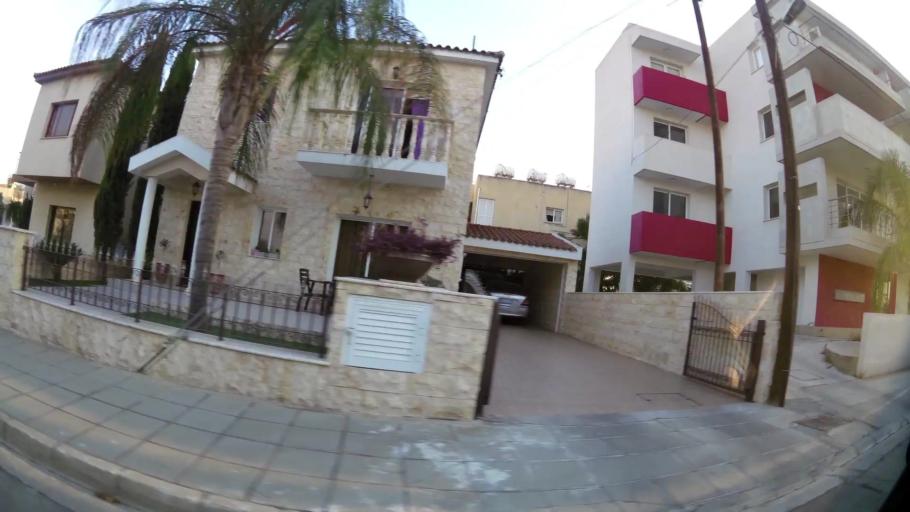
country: CY
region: Larnaka
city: Larnaca
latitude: 34.9162
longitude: 33.5944
